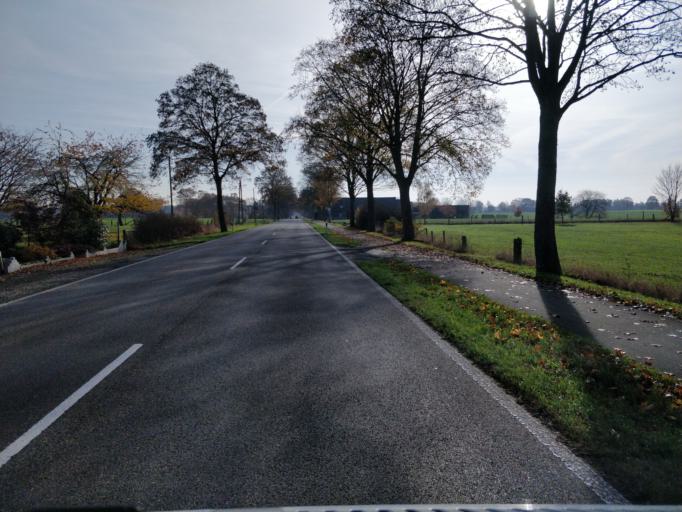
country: DE
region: North Rhine-Westphalia
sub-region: Regierungsbezirk Dusseldorf
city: Mehrhoog
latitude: 51.7309
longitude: 6.5042
